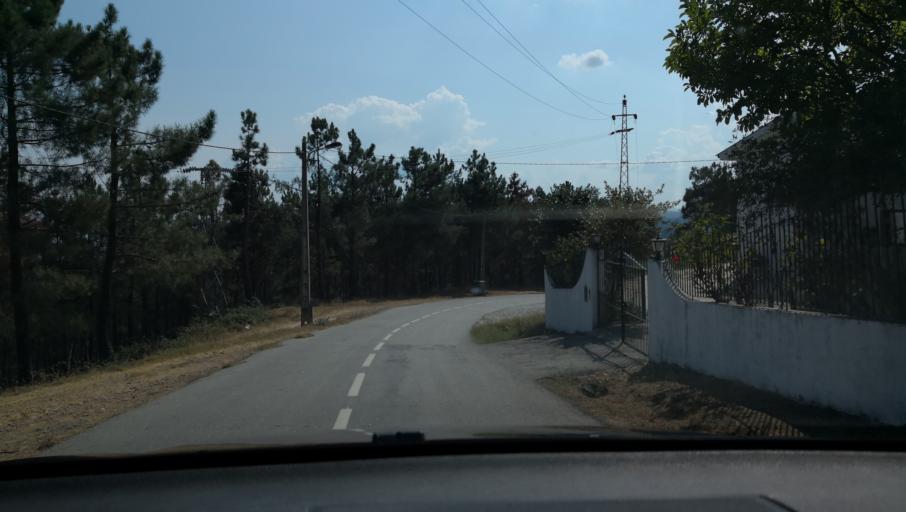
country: PT
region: Vila Real
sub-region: Sabrosa
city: Sabrosa
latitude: 41.2736
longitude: -7.6174
